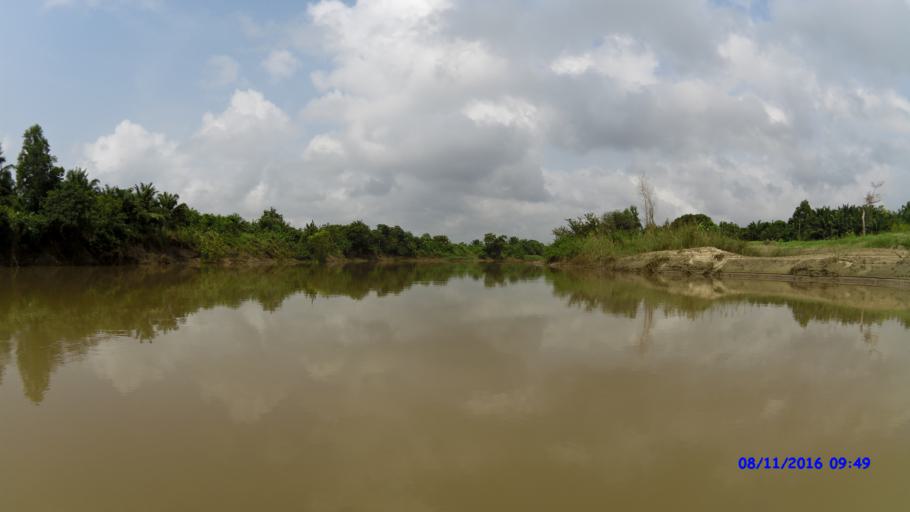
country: BJ
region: Mono
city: Come
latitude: 6.4307
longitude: 1.7679
